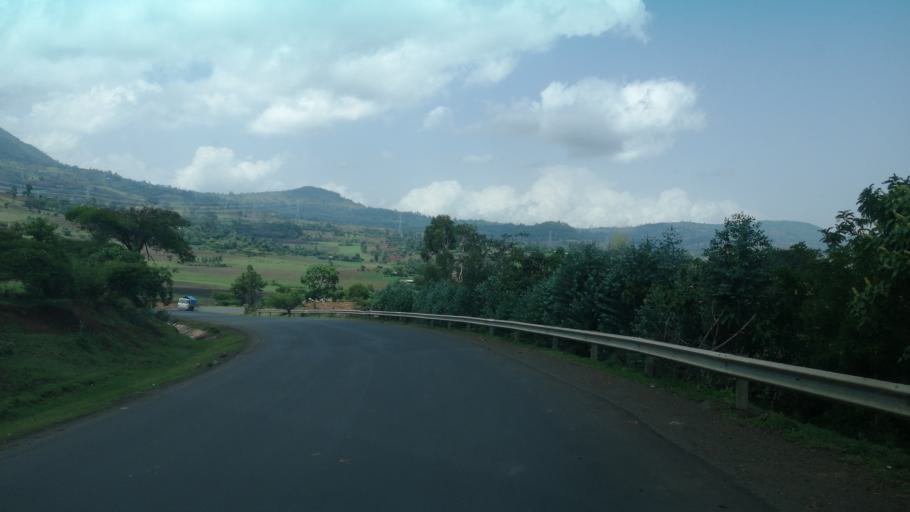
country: ET
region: Oromiya
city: Gedo
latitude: 8.9764
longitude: 37.5588
